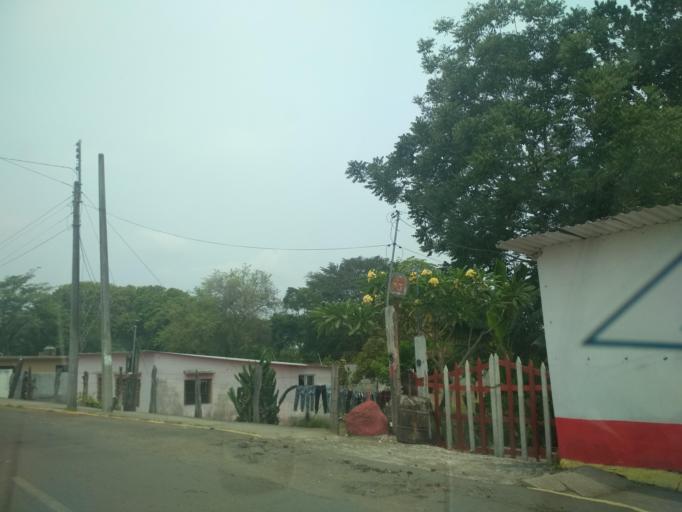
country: MX
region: Veracruz
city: El Tejar
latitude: 19.0583
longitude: -96.1587
